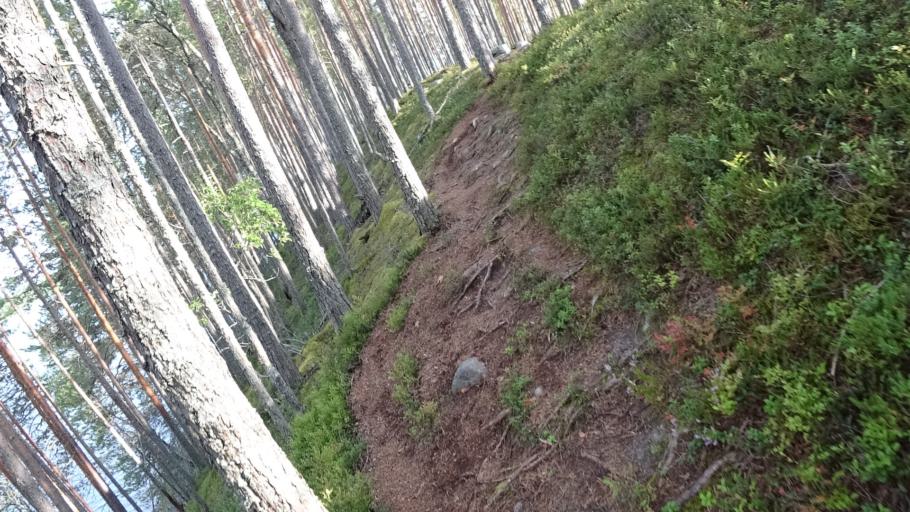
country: FI
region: North Karelia
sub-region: Joensuu
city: Ilomantsi
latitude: 62.5688
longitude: 31.1802
